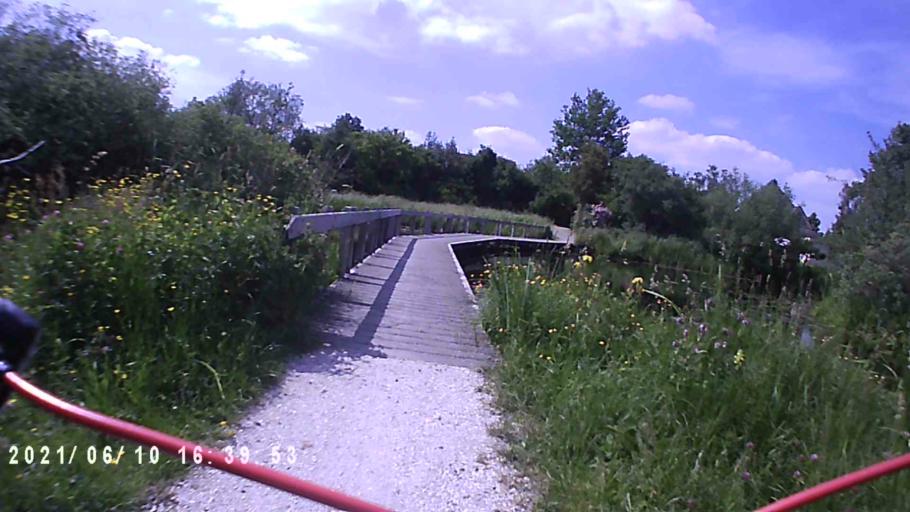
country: NL
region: Friesland
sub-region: Gemeente Achtkarspelen
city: Buitenpost
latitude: 53.2433
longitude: 6.1424
